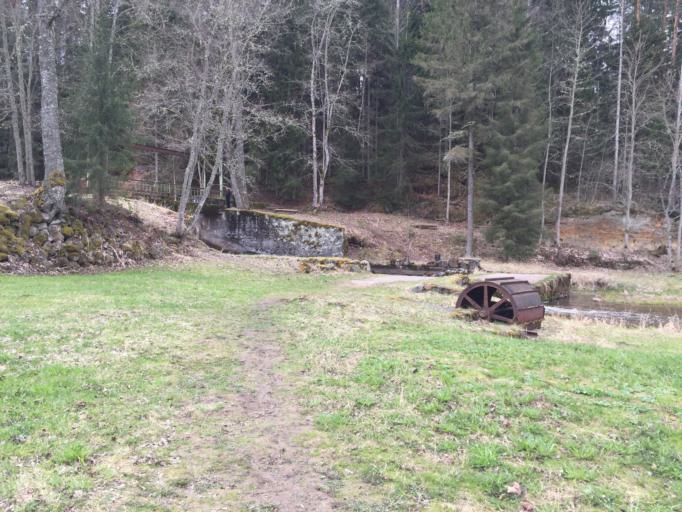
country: LV
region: Priekuli
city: Priekuli
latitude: 57.3307
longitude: 25.3927
